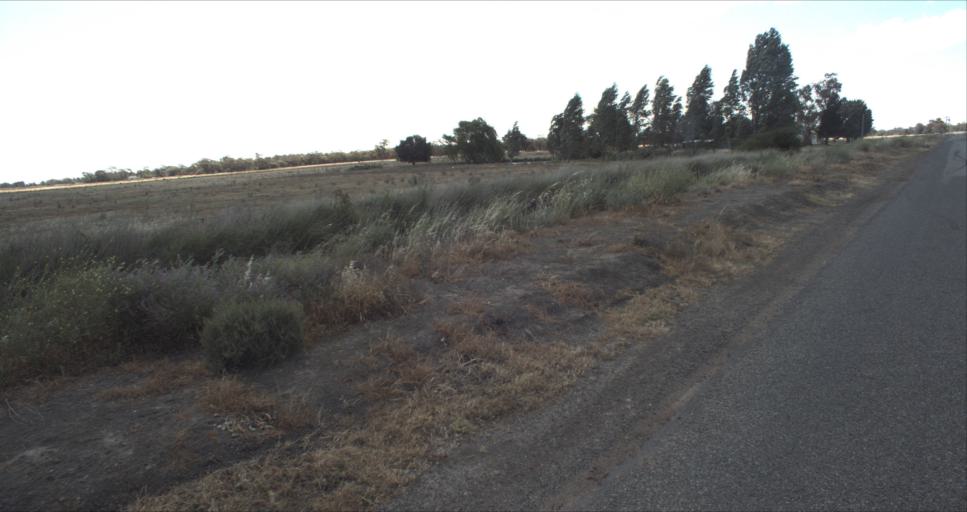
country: AU
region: New South Wales
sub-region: Leeton
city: Leeton
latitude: -34.5268
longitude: 146.2206
